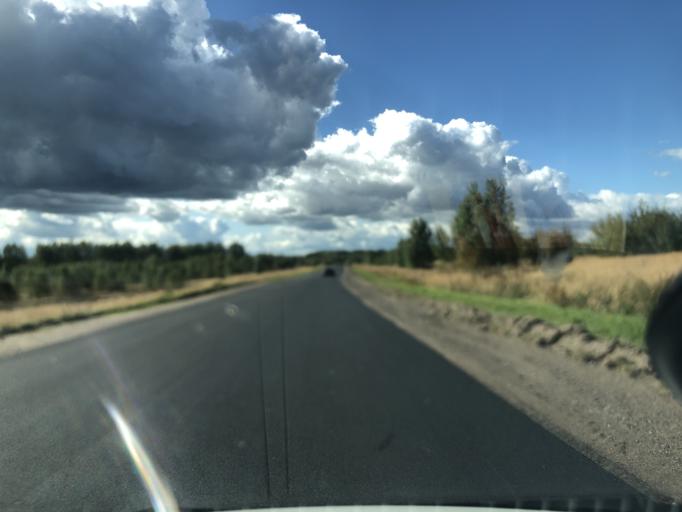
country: RU
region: Jaroslavl
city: Petrovsk
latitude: 56.9563
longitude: 39.3489
